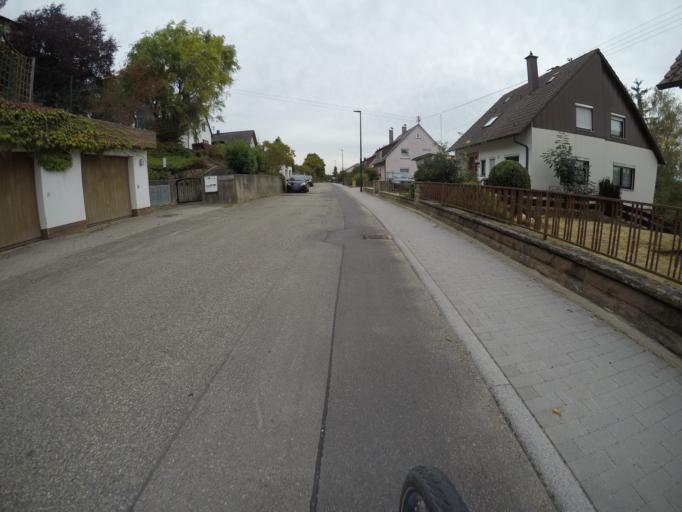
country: DE
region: Baden-Wuerttemberg
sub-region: Karlsruhe Region
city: Muhlacker
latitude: 48.9749
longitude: 8.8660
